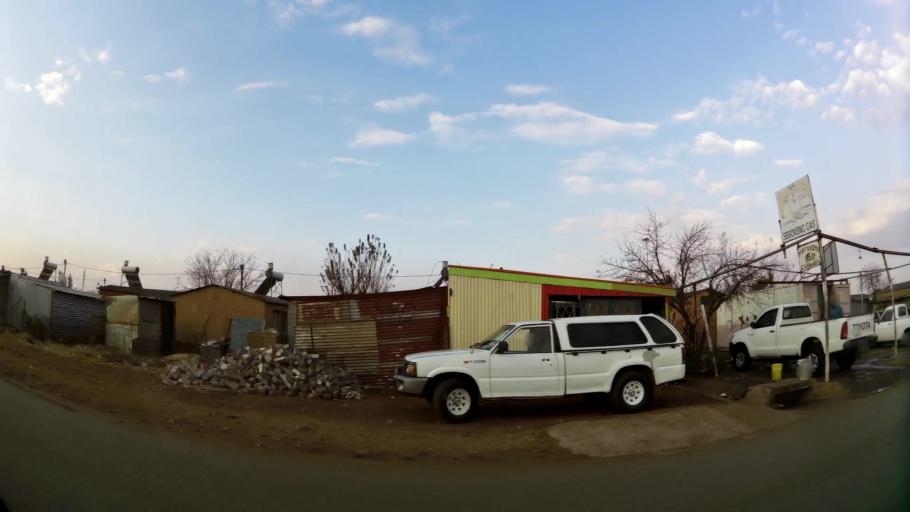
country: ZA
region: Gauteng
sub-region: City of Johannesburg Metropolitan Municipality
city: Orange Farm
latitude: -26.5588
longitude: 27.8315
